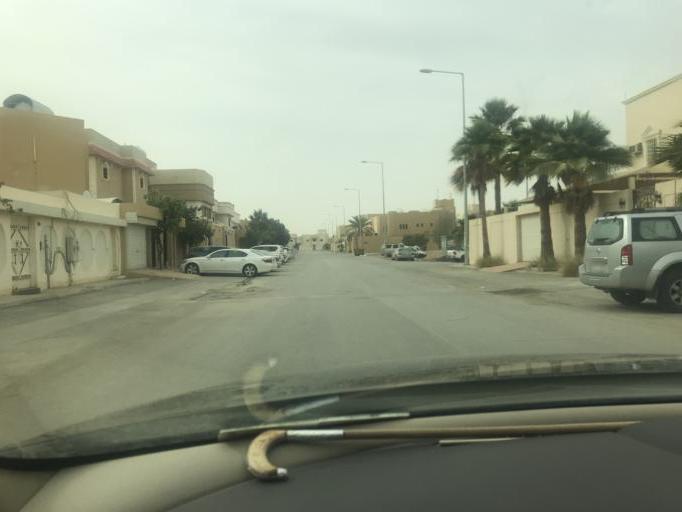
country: SA
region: Ar Riyad
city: Riyadh
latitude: 24.7532
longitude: 46.7640
